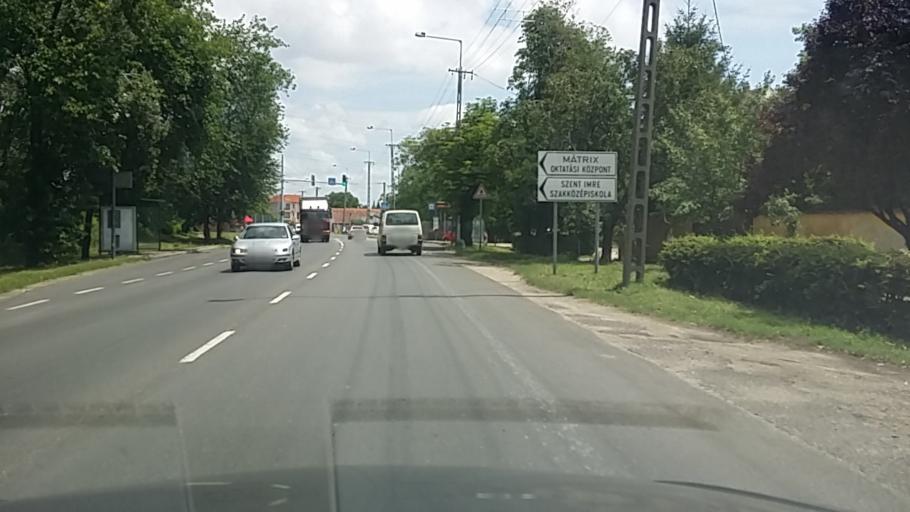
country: HU
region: Bacs-Kiskun
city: Kecskemet
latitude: 46.8913
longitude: 19.6560
